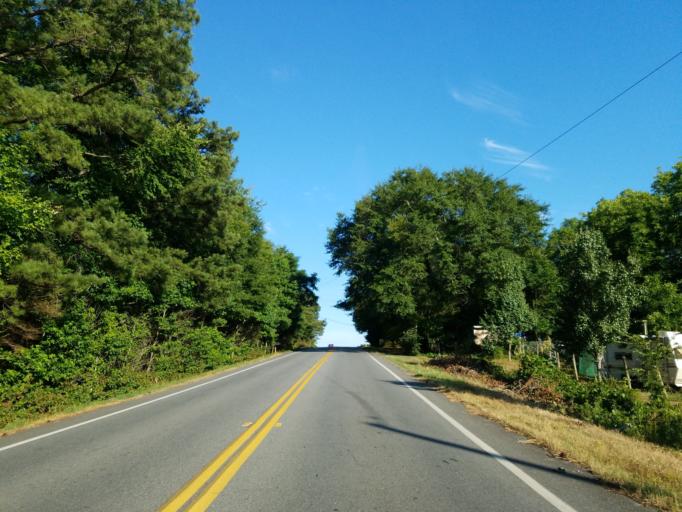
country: US
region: Georgia
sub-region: Gordon County
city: Calhoun
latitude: 34.5565
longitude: -85.0107
